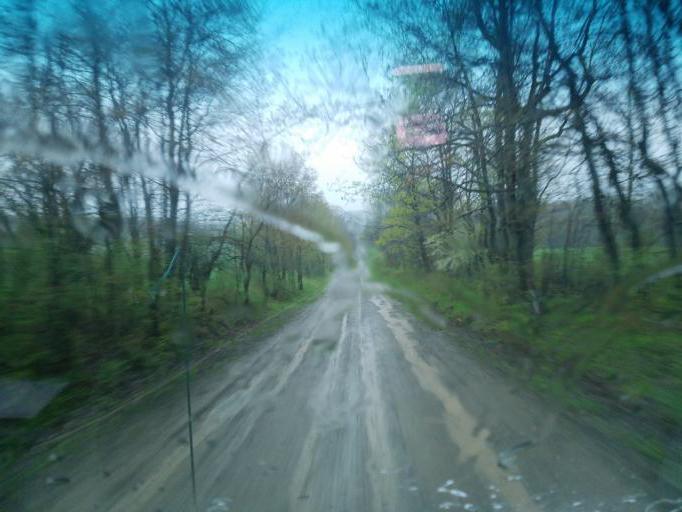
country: US
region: Pennsylvania
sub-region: Tioga County
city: Westfield
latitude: 41.9206
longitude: -77.7295
